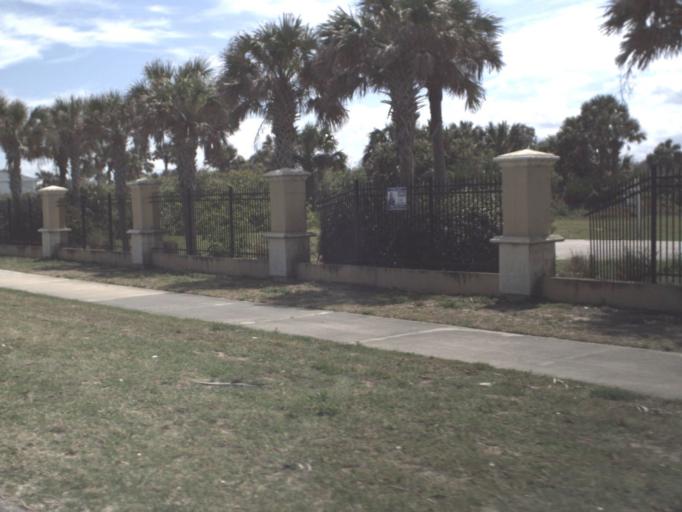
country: US
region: Florida
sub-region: Flagler County
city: Palm Coast
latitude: 29.5478
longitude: -81.1610
